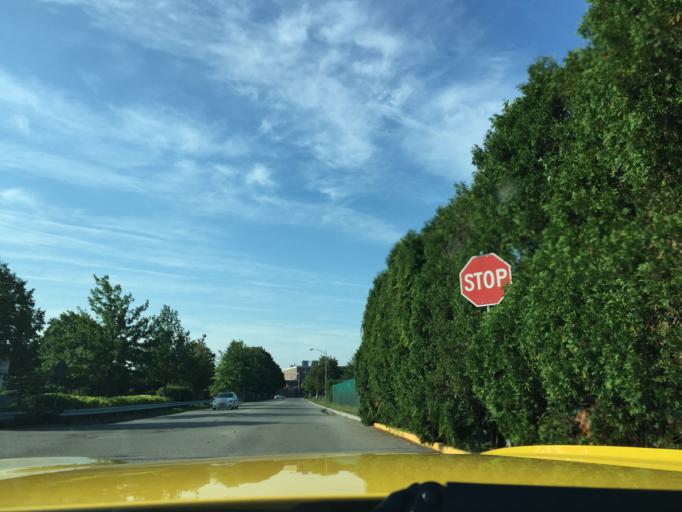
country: US
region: New York
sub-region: Nassau County
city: Hicksville
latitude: 40.7703
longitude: -73.5336
